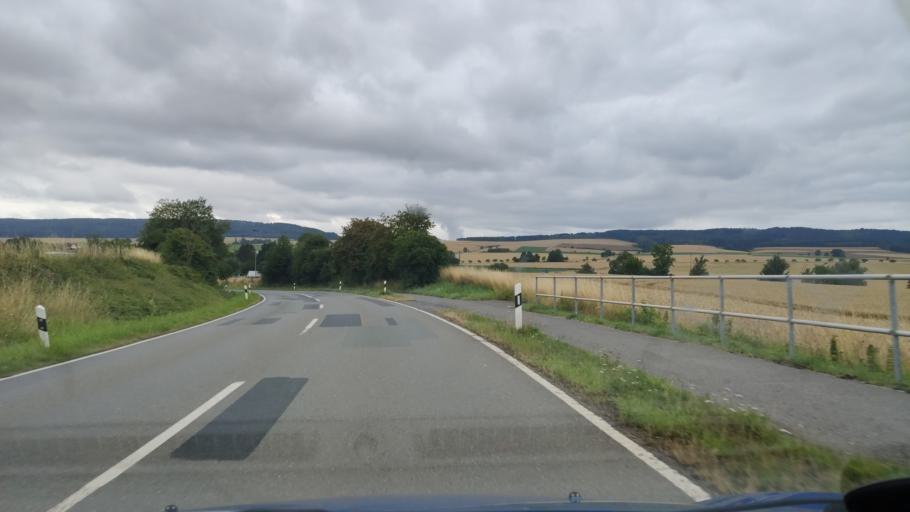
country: DE
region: Lower Saxony
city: Coppenbrugge
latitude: 52.0963
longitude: 9.4946
